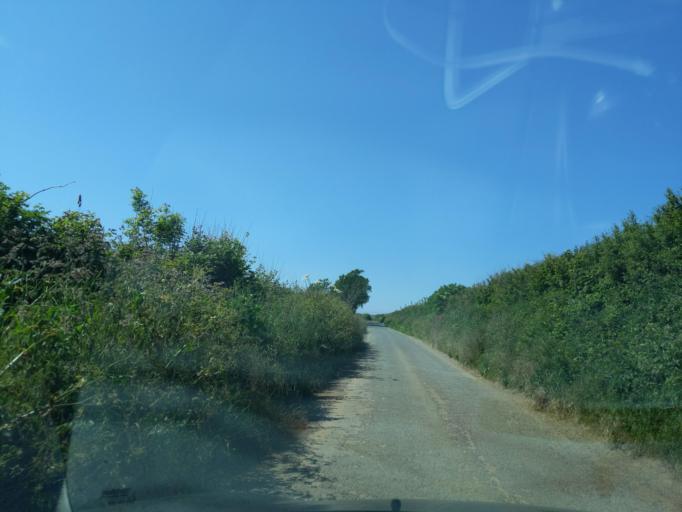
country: GB
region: England
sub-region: Cornwall
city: Wadebridge
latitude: 50.5794
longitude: -4.8324
